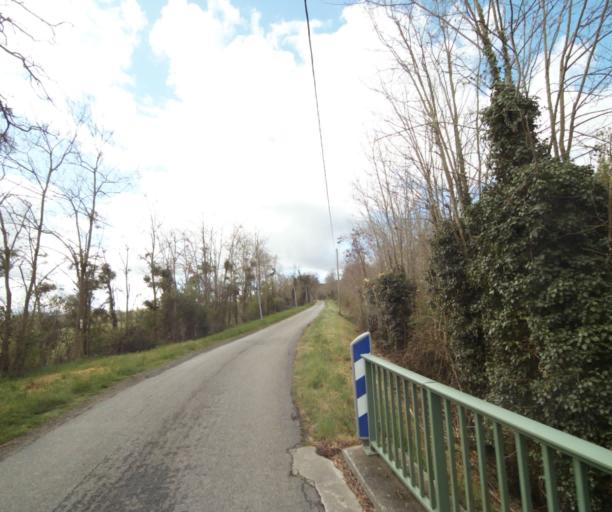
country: FR
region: Midi-Pyrenees
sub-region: Departement de l'Ariege
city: Saverdun
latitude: 43.2095
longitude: 1.5758
